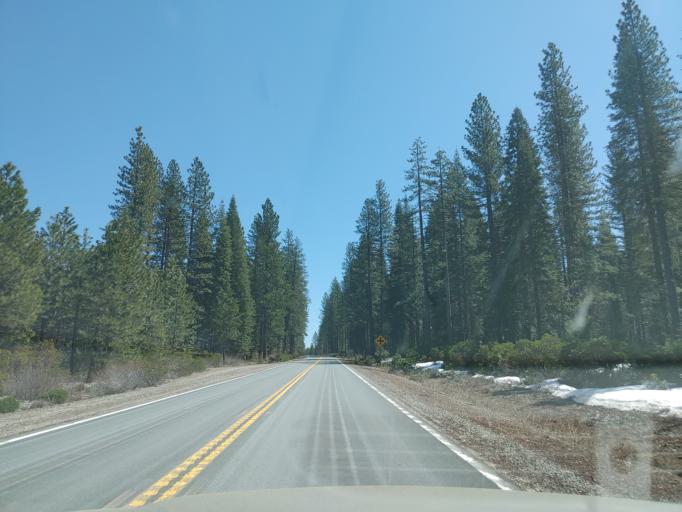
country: US
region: California
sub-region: Siskiyou County
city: McCloud
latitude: 41.2666
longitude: -121.8884
